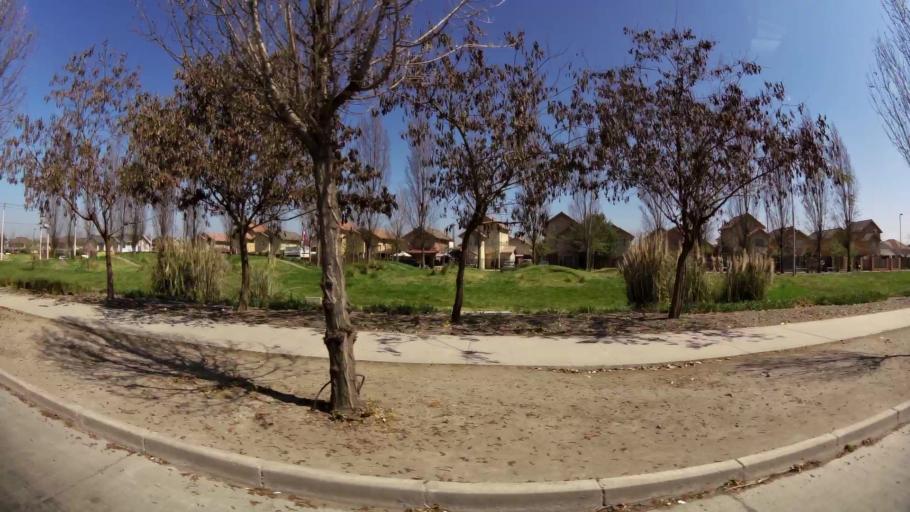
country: CL
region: Santiago Metropolitan
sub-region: Provincia de Chacabuco
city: Chicureo Abajo
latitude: -33.3281
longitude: -70.7461
